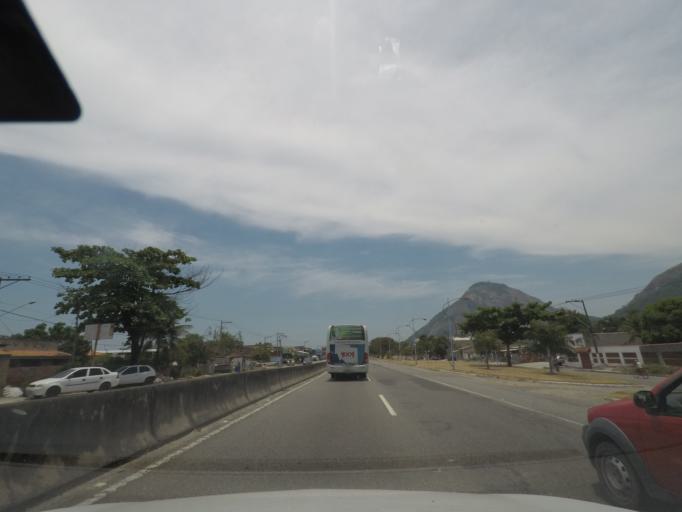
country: BR
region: Rio de Janeiro
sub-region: Marica
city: Marica
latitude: -22.9320
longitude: -42.8848
